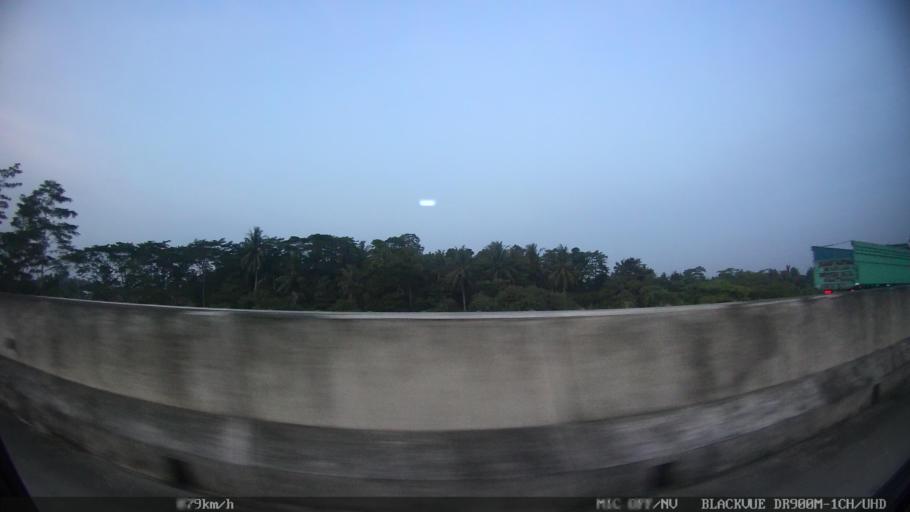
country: ID
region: Lampung
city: Kalianda
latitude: -5.6704
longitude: 105.6009
